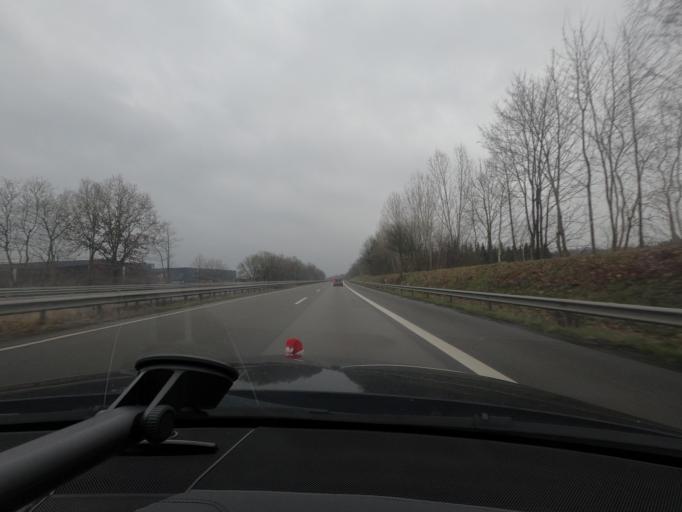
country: DE
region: Lower Saxony
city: Seevetal
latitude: 53.3898
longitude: 10.0010
